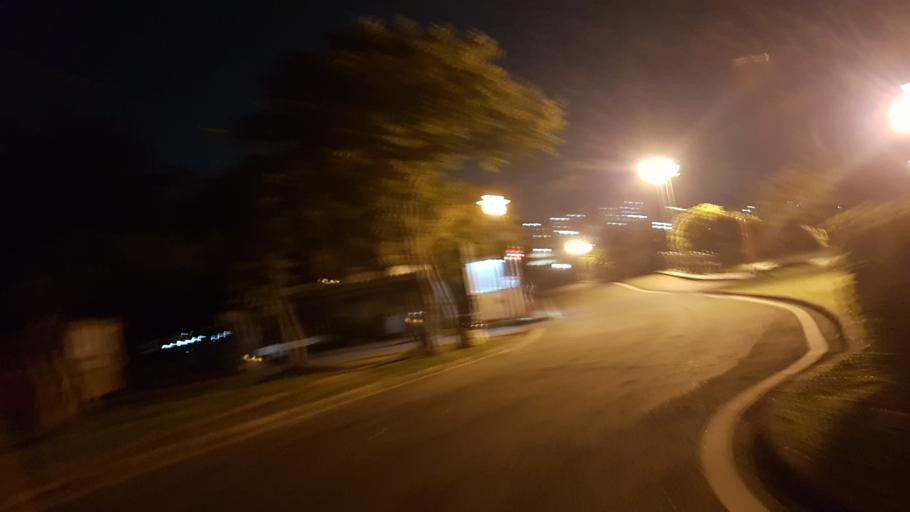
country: TW
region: Taipei
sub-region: Taipei
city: Banqiao
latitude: 24.9777
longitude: 121.5181
